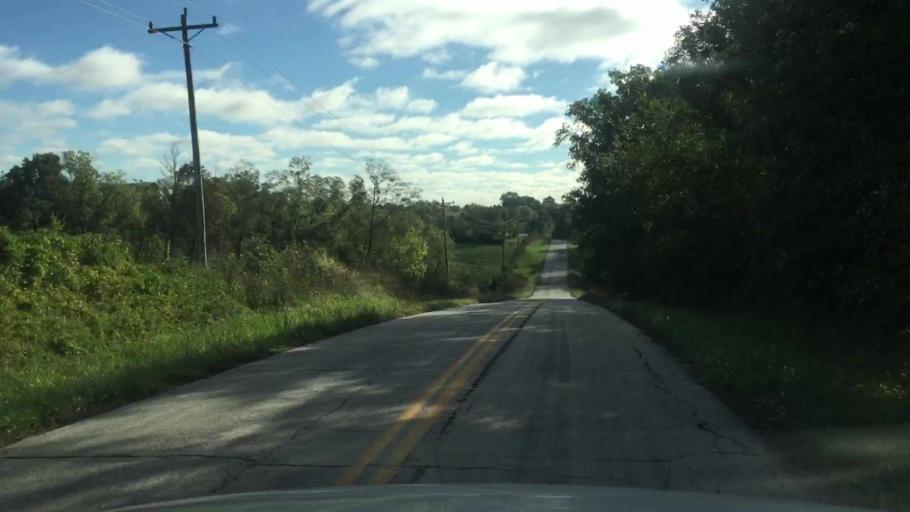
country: US
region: Missouri
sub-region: Howard County
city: New Franklin
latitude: 39.1051
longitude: -92.7767
